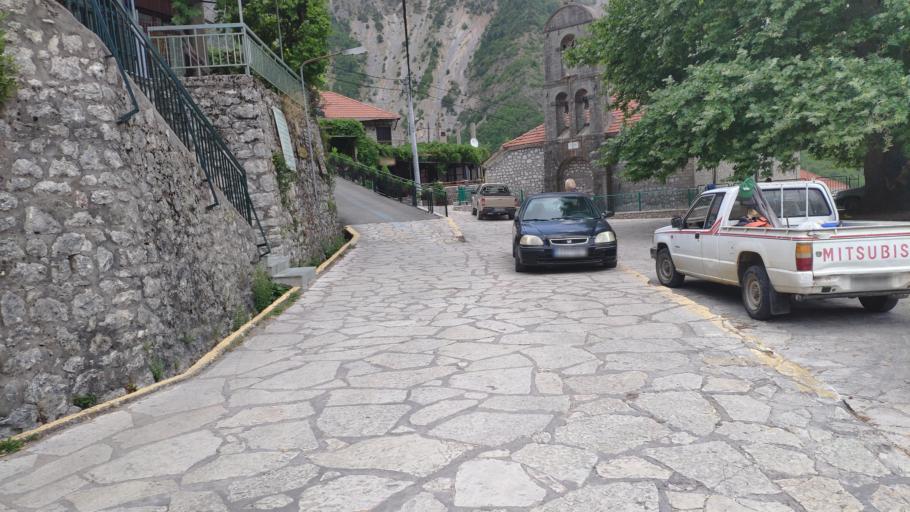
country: GR
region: Epirus
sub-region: Nomos Artas
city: Voulgareli
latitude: 39.4343
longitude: 21.2094
